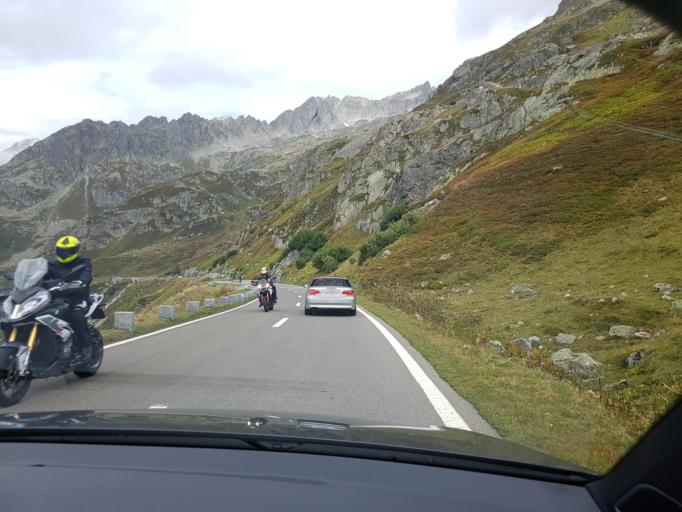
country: CH
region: Obwalden
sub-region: Obwalden
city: Engelberg
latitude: 46.7282
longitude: 8.4411
